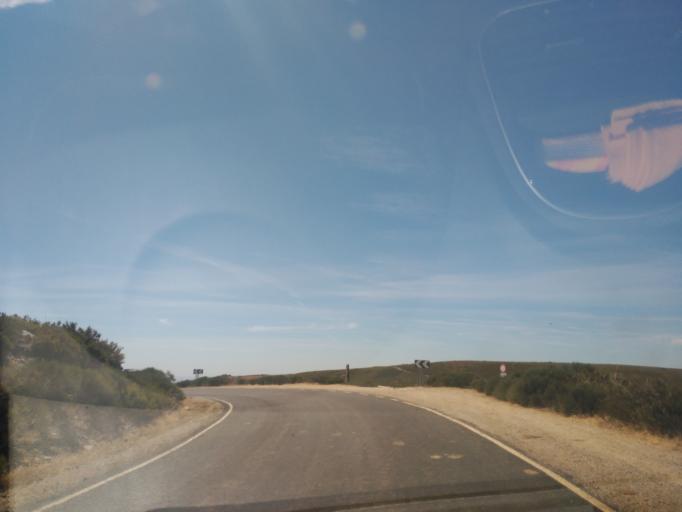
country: ES
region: Castille and Leon
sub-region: Provincia de Zamora
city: Trefacio
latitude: 42.1653
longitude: -6.7350
